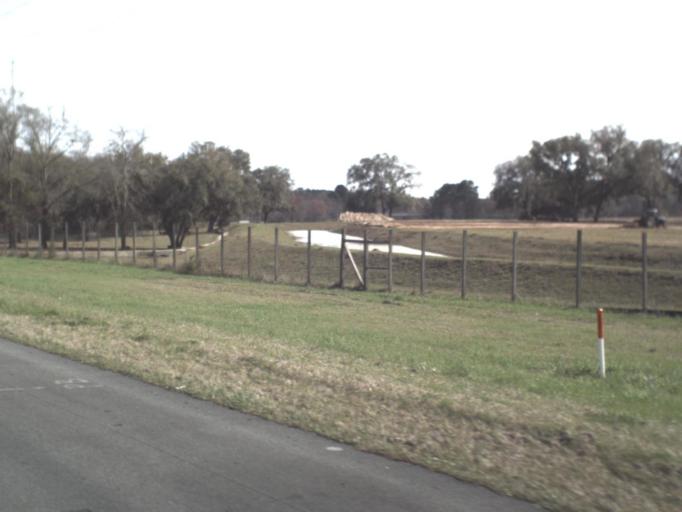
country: US
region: Florida
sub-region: Leon County
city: Tallahassee
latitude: 30.4901
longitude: -84.1661
